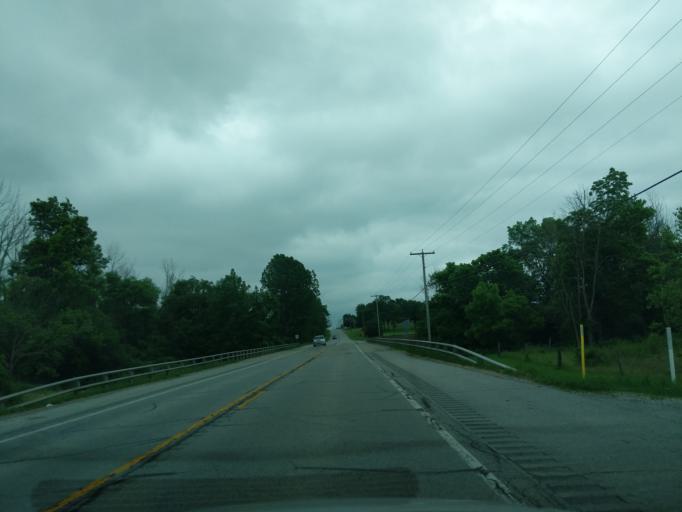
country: US
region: Indiana
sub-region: Madison County
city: Alexandria
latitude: 40.2773
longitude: -85.6913
